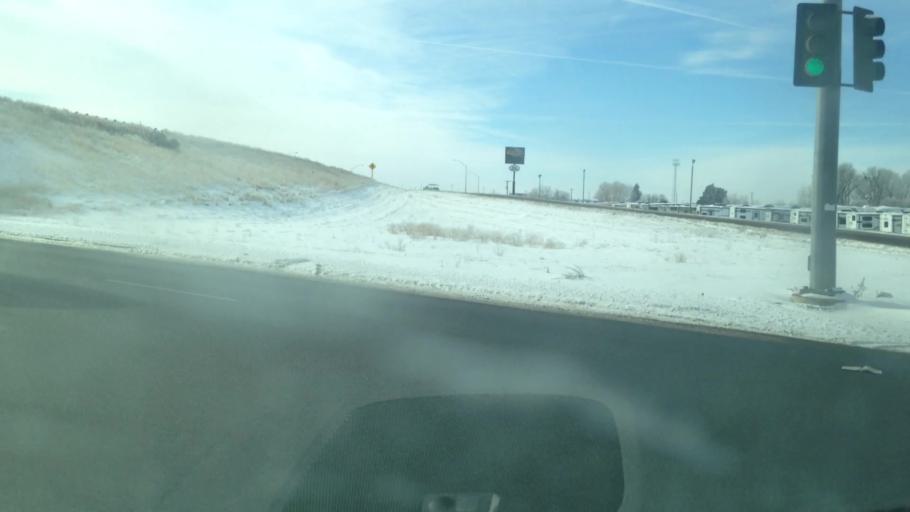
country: US
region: Idaho
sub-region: Bonneville County
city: Lincoln
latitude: 43.5278
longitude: -112.0236
